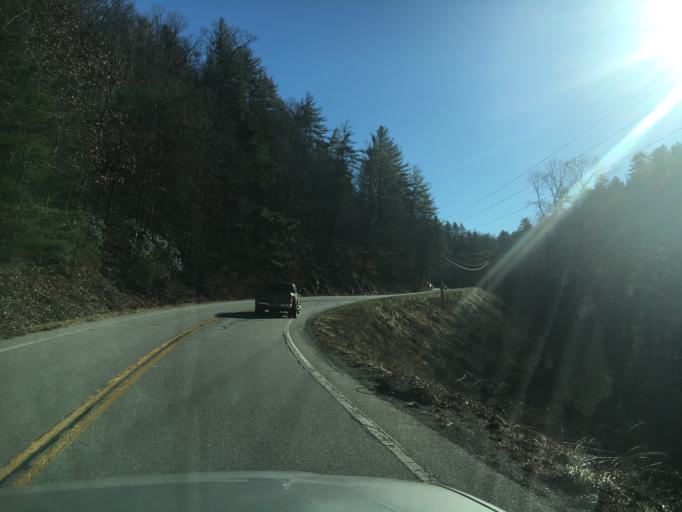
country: US
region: Georgia
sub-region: Union County
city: Blairsville
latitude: 34.7877
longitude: -83.9060
